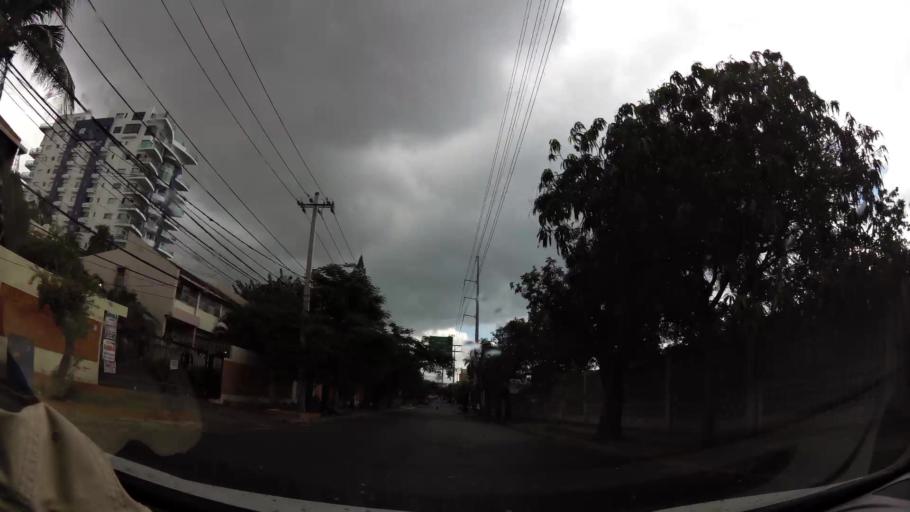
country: DO
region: Nacional
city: Ciudad Nueva
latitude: 18.4652
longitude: -69.9152
